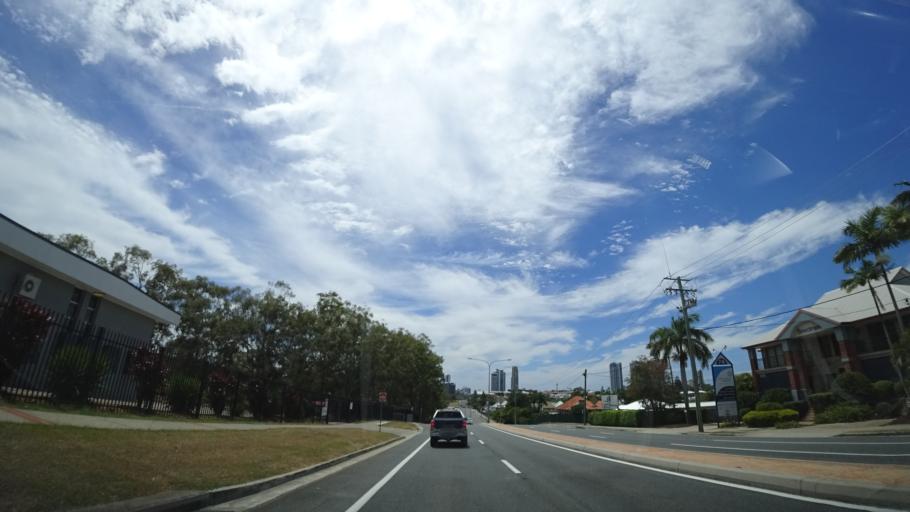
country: AU
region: Queensland
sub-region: Gold Coast
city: Southport
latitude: -27.9629
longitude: 153.4025
